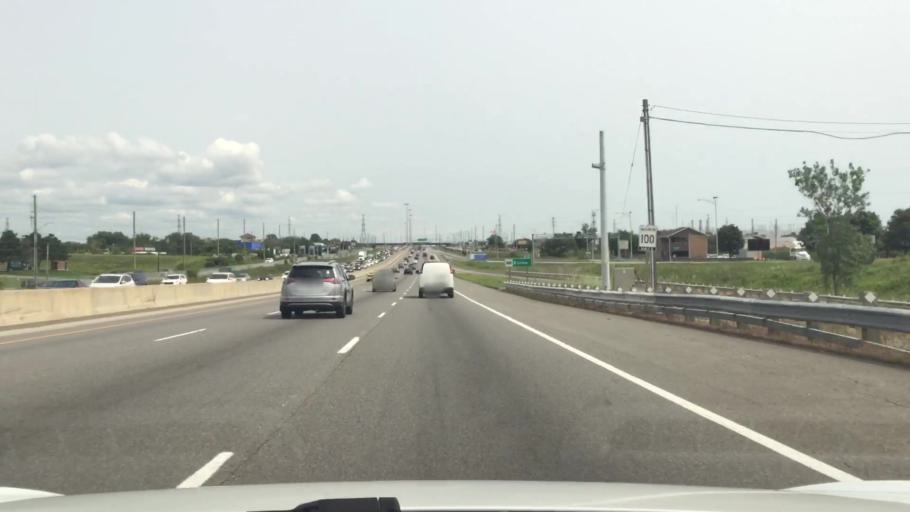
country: CA
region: Ontario
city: Oshawa
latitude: 43.8699
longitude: -78.8969
